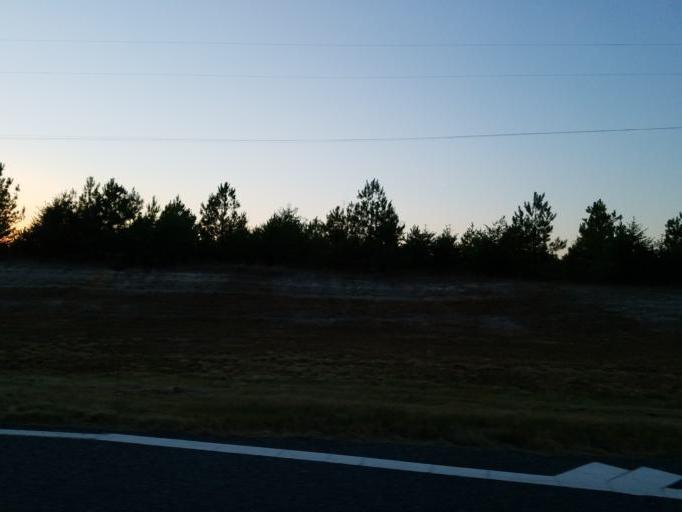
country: US
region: Georgia
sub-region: Dawson County
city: Dawsonville
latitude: 34.3134
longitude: -84.0650
